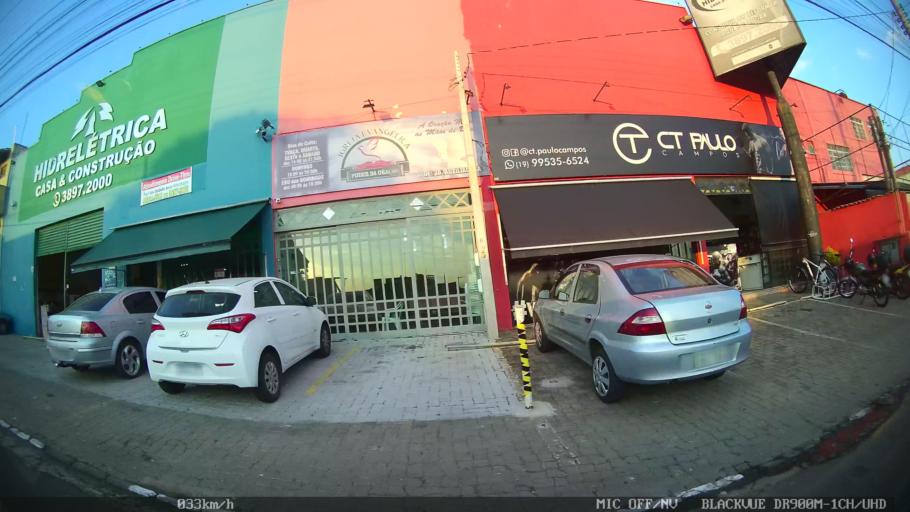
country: BR
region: Sao Paulo
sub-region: Hortolandia
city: Hortolandia
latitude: -22.8553
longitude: -47.2059
